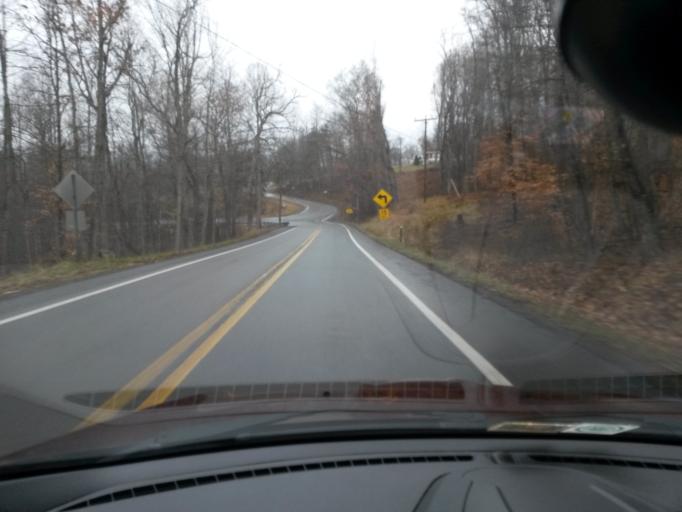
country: US
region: West Virginia
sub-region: Greenbrier County
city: Lewisburg
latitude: 37.8717
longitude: -80.5503
